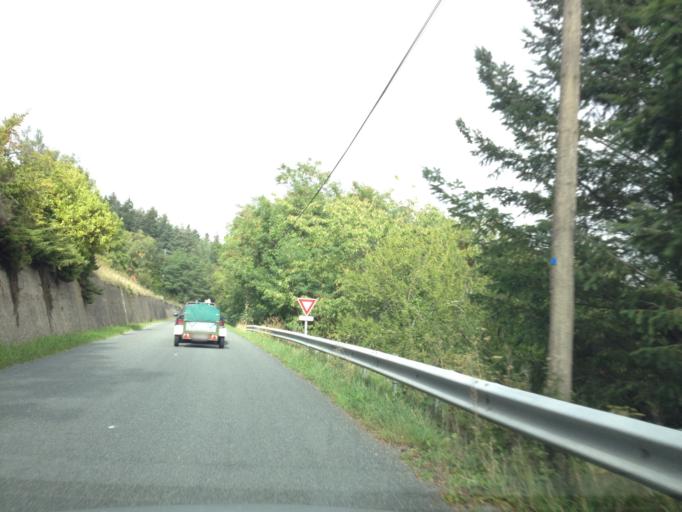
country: FR
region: Rhone-Alpes
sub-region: Departement de la Loire
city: Renaison
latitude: 46.0488
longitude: 3.9083
